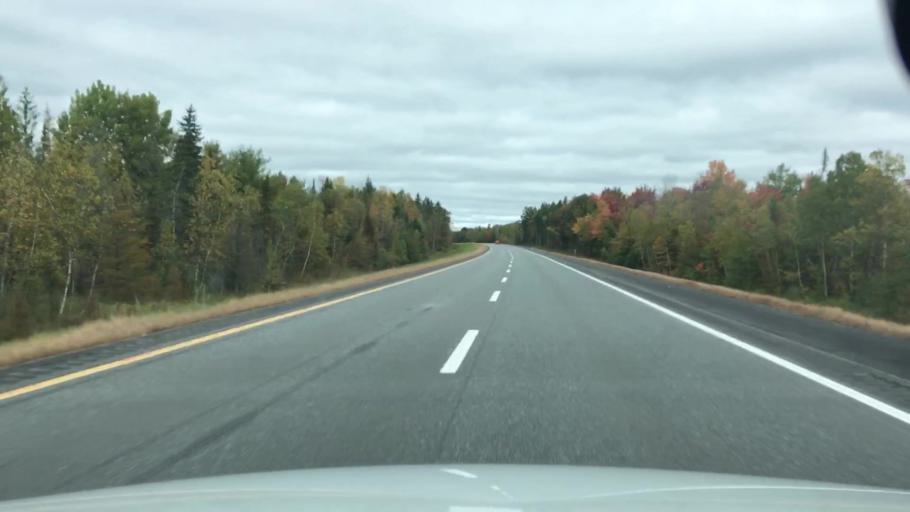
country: US
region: Maine
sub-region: Waldo County
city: Burnham
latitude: 44.7082
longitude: -69.4520
